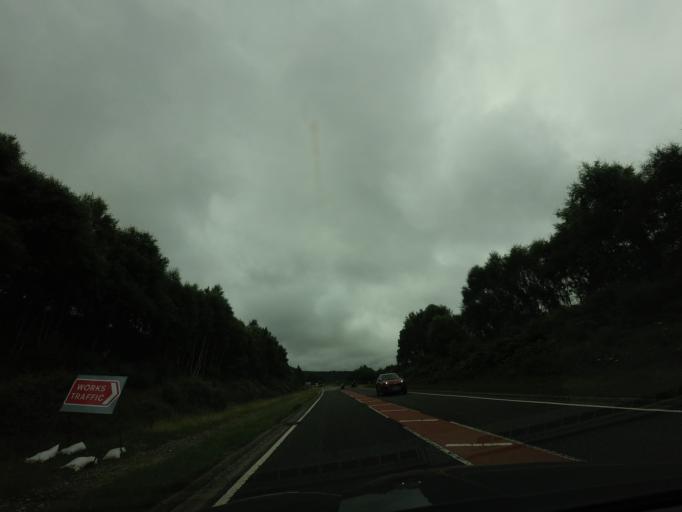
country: GB
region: Scotland
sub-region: Highland
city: Aviemore
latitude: 57.2967
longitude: -3.9211
